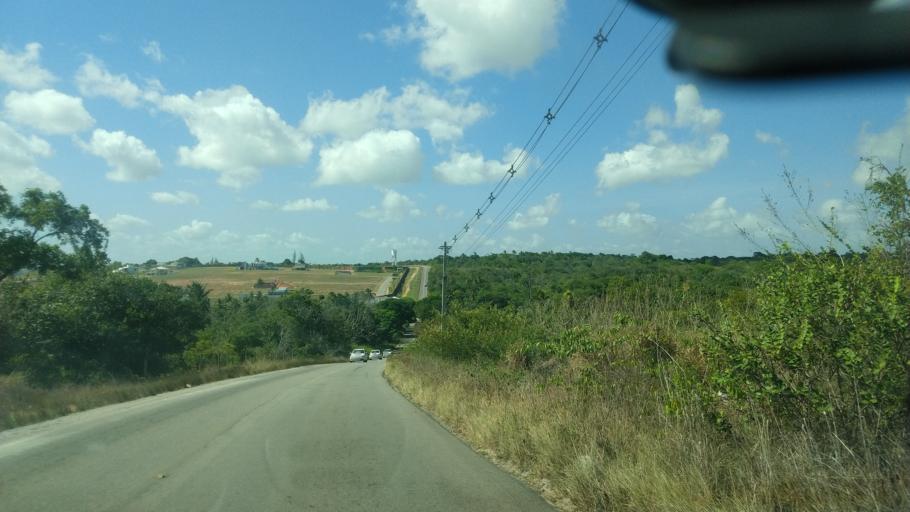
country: BR
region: Rio Grande do Norte
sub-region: Parnamirim
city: Parnamirim
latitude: -5.9506
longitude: -35.2351
